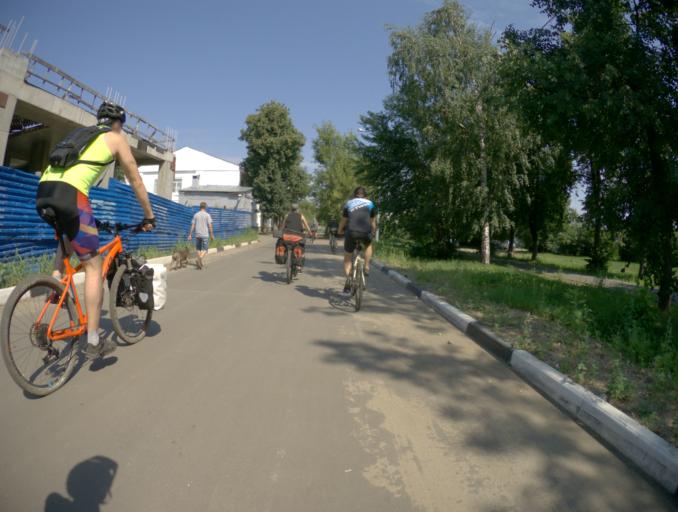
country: RU
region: Nizjnij Novgorod
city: Nizhniy Novgorod
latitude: 56.3194
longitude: 43.9558
